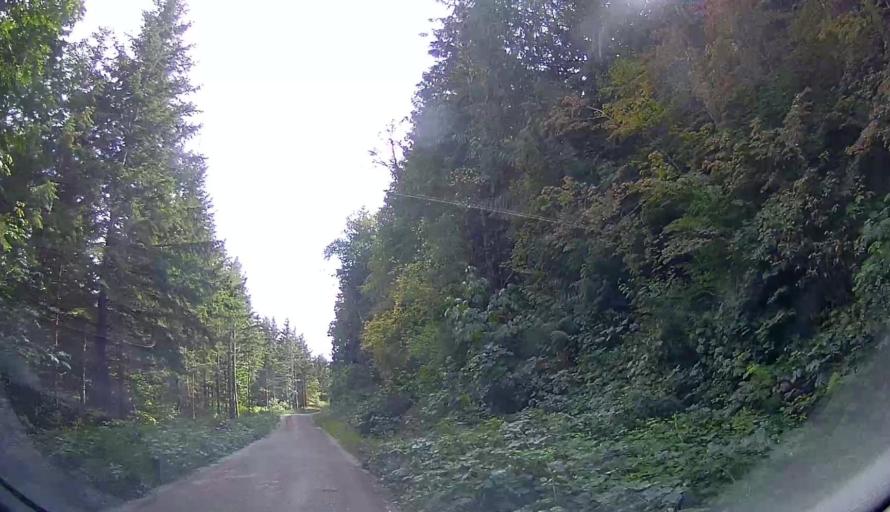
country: US
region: Washington
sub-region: Whatcom County
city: Sudden Valley
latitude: 48.6159
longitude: -122.3804
